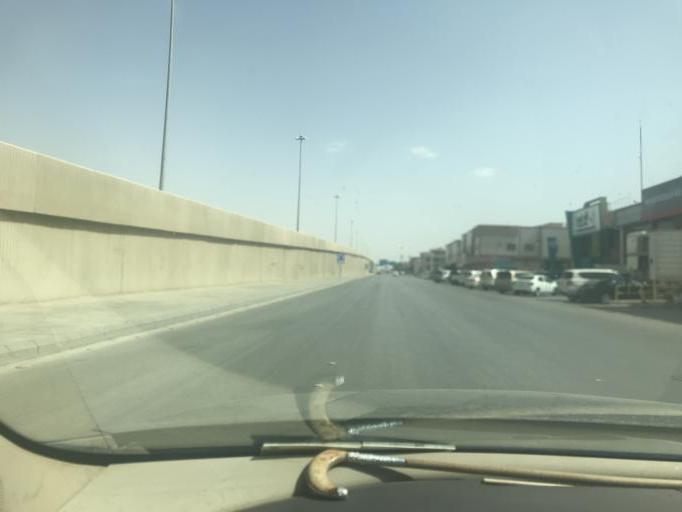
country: SA
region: Ar Riyad
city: Riyadh
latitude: 24.7929
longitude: 46.7002
